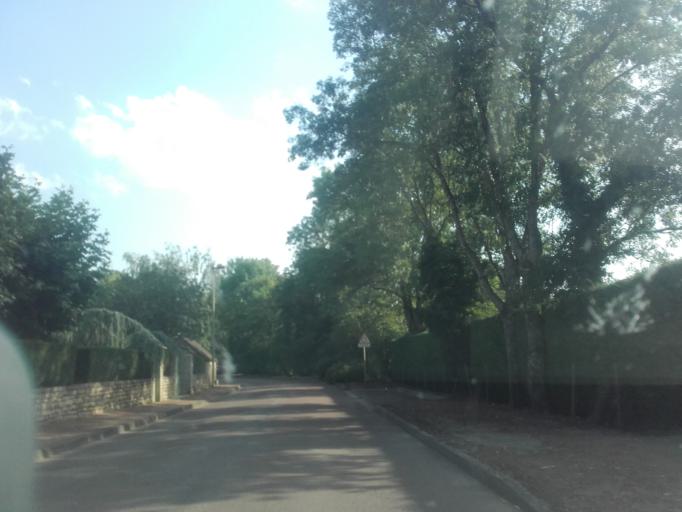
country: FR
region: Bourgogne
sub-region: Departement de la Cote-d'Or
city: Bligny-les-Beaune
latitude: 46.9931
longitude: 4.8508
